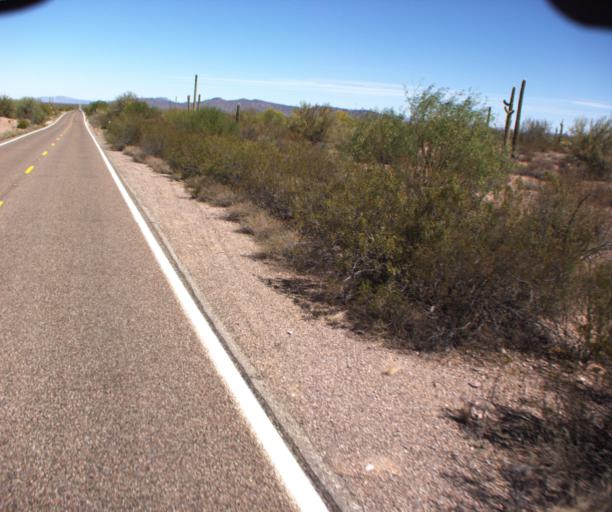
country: MX
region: Sonora
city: Sonoyta
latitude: 32.1097
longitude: -112.7700
